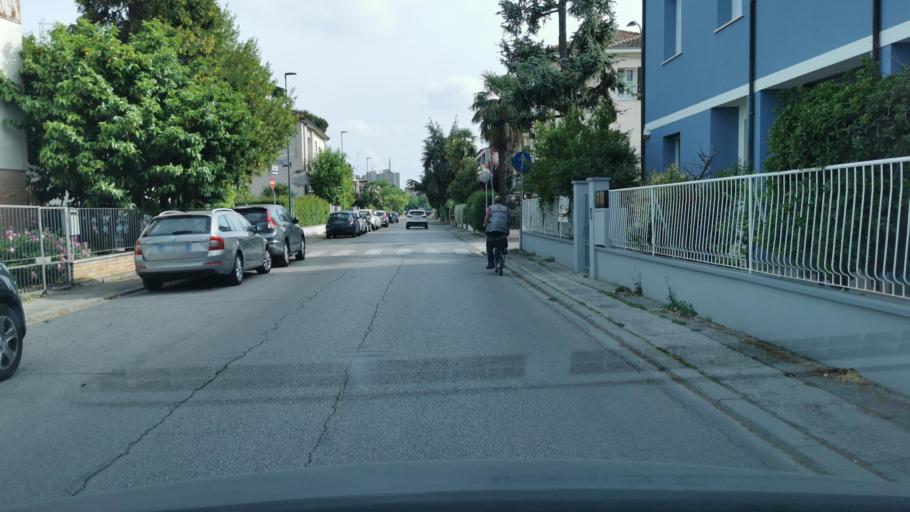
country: IT
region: Emilia-Romagna
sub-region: Provincia di Ravenna
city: Ravenna
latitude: 44.4069
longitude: 12.2050
